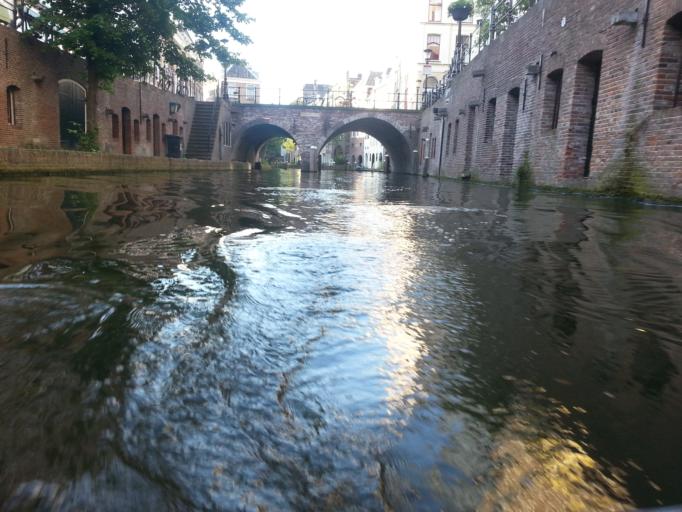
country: NL
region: Utrecht
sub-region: Gemeente Utrecht
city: Utrecht
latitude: 52.0908
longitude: 5.1202
